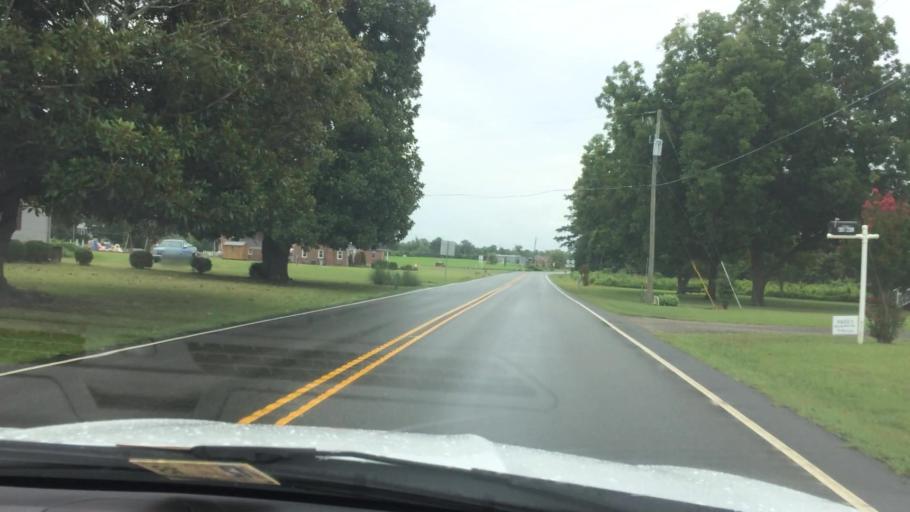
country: US
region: Virginia
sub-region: King William County
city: West Point
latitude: 37.5523
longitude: -76.7358
